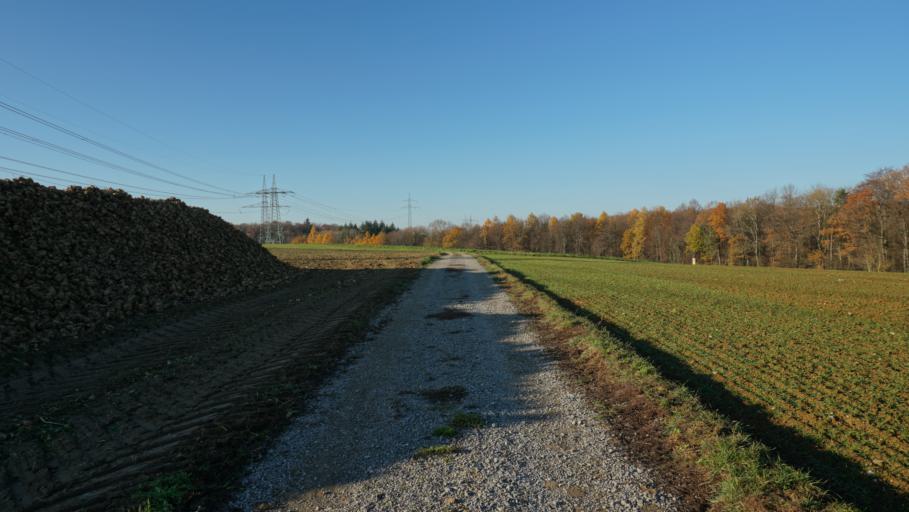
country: DE
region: Baden-Wuerttemberg
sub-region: Karlsruhe Region
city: Huffenhardt
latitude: 49.2978
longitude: 9.0939
